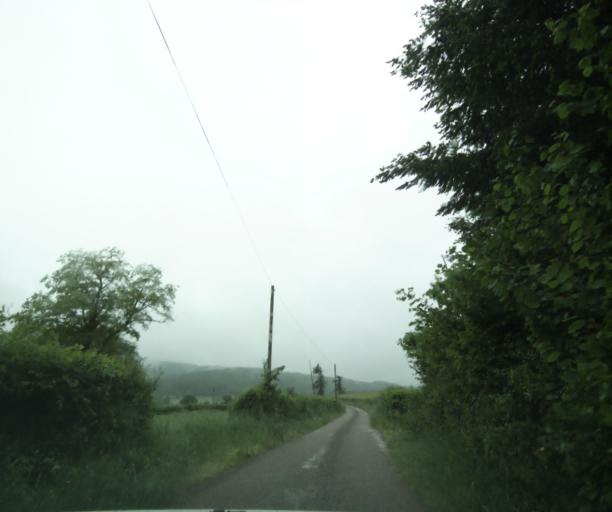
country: FR
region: Bourgogne
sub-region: Departement de Saone-et-Loire
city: La Clayette
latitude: 46.3676
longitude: 4.3804
